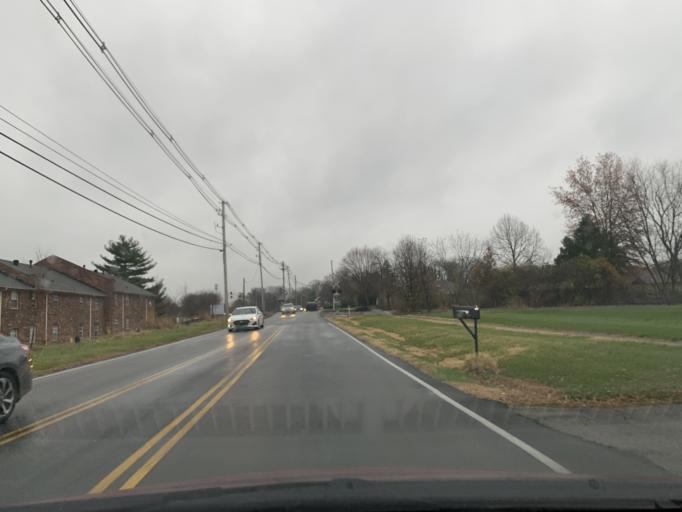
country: US
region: Kentucky
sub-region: Jefferson County
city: Saint Regis Park
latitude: 38.2001
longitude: -85.6131
